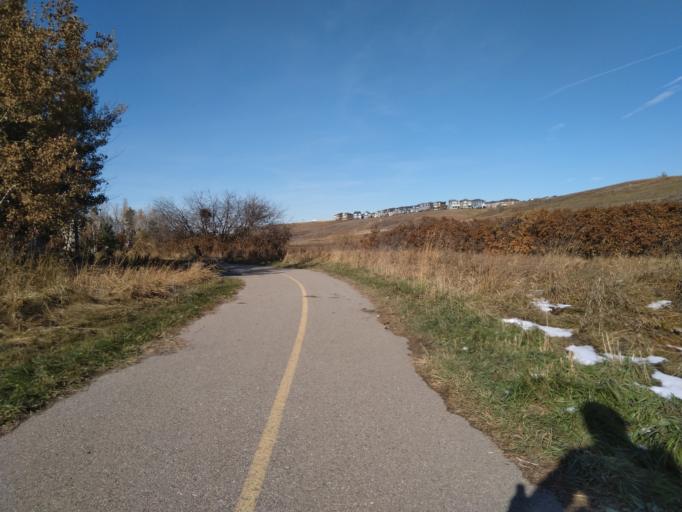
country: CA
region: Alberta
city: Calgary
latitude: 51.1749
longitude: -114.1284
